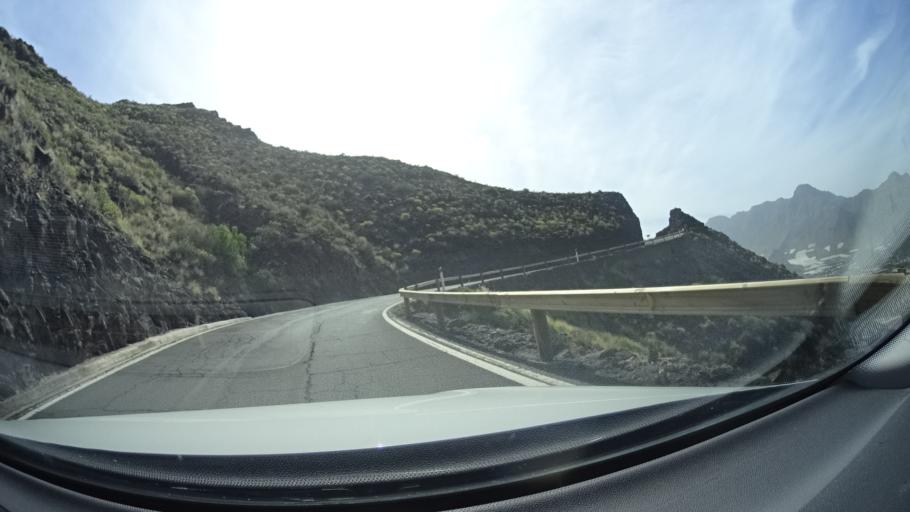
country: ES
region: Canary Islands
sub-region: Provincia de Las Palmas
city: San Nicolas
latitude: 28.0133
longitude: -15.7857
